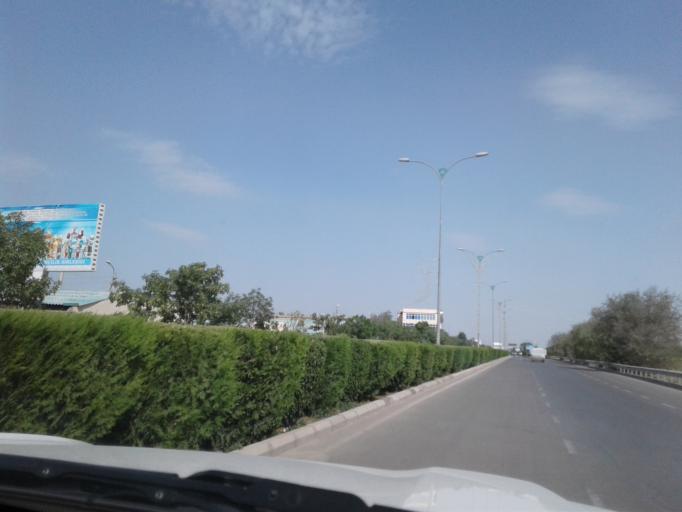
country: TM
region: Dasoguz
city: Dasoguz
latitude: 41.8311
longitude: 59.9414
